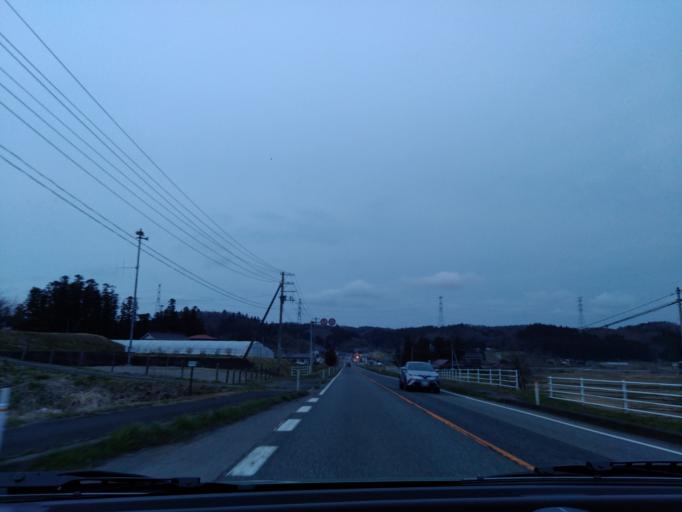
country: JP
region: Iwate
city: Ichinoseki
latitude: 38.8458
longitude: 141.0946
